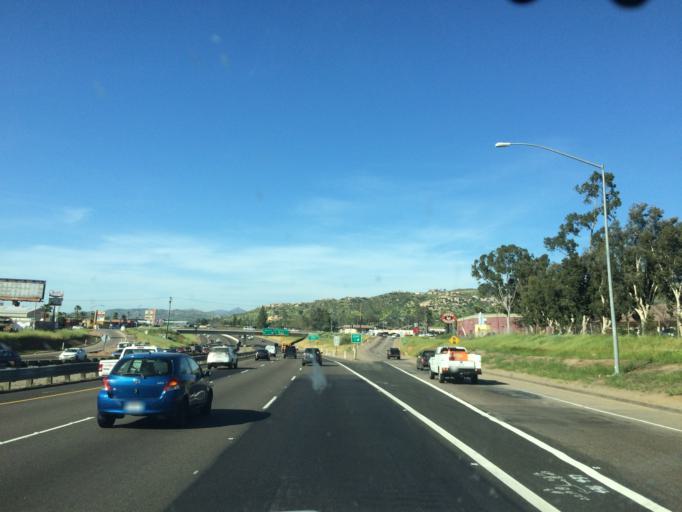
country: US
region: California
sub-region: San Diego County
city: El Cajon
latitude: 32.8165
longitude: -116.9608
